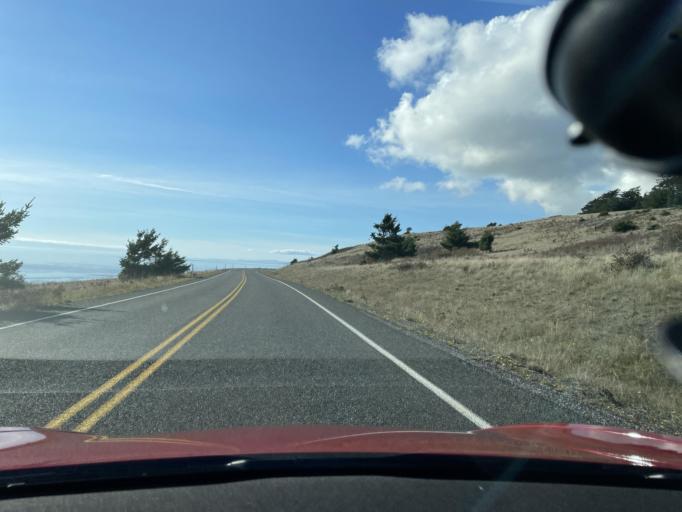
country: US
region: Washington
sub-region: San Juan County
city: Friday Harbor
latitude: 48.4569
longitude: -122.9860
